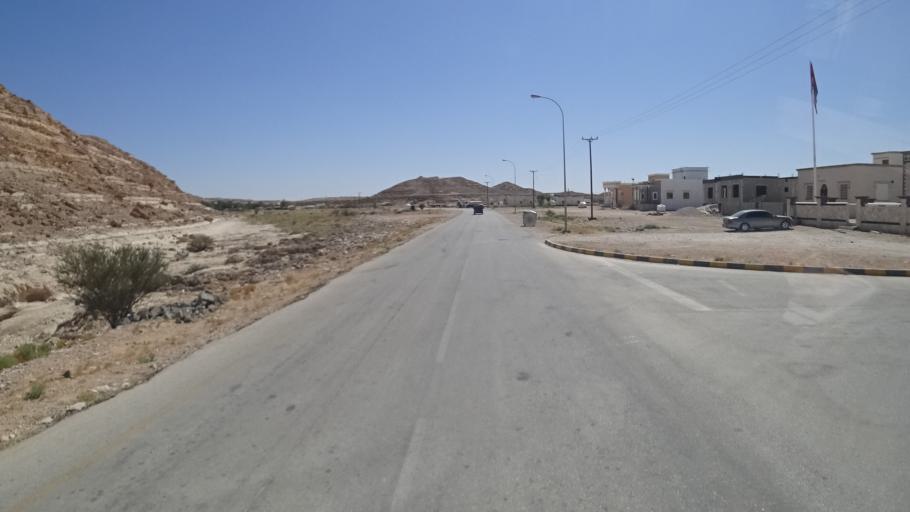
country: OM
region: Zufar
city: Salalah
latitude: 17.4849
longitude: 53.3491
